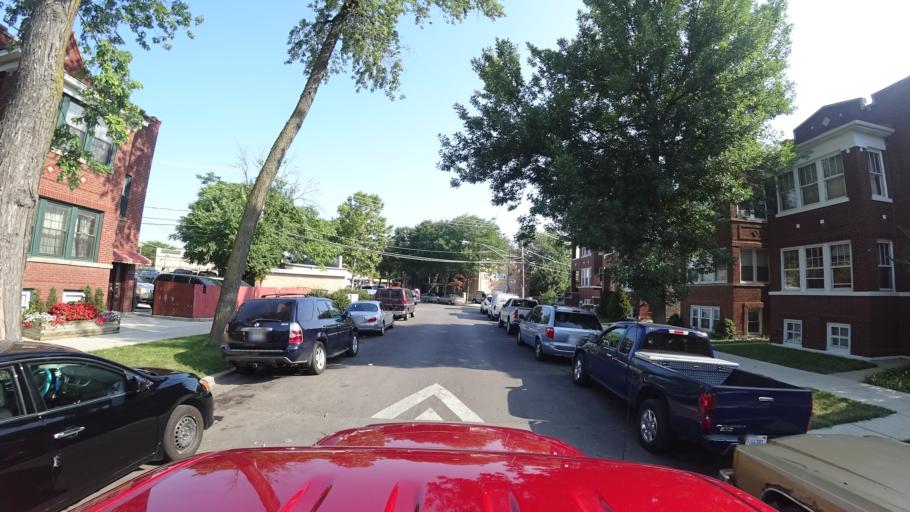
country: US
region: Illinois
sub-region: Cook County
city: Cicero
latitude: 41.8109
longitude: -87.7078
